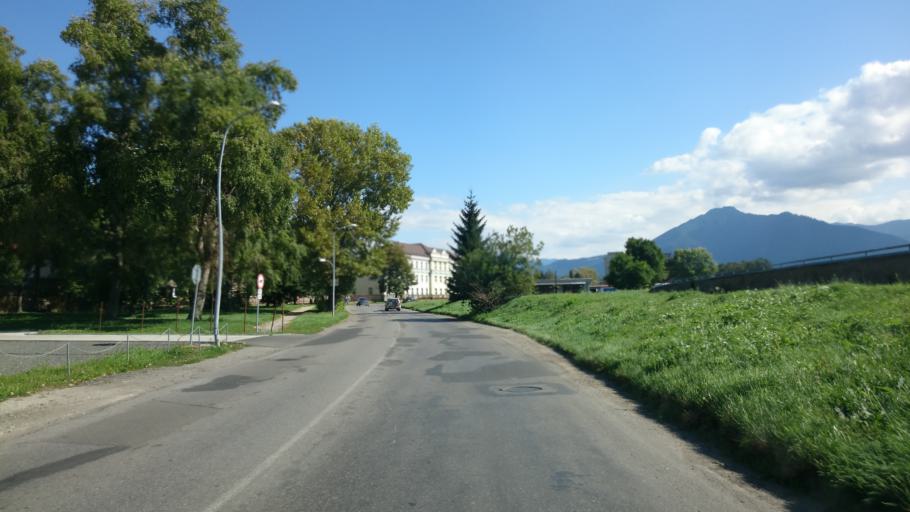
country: SK
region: Zilinsky
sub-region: Okres Liptovsky Mikulas
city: Liptovsky Mikulas
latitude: 49.0907
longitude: 19.6006
